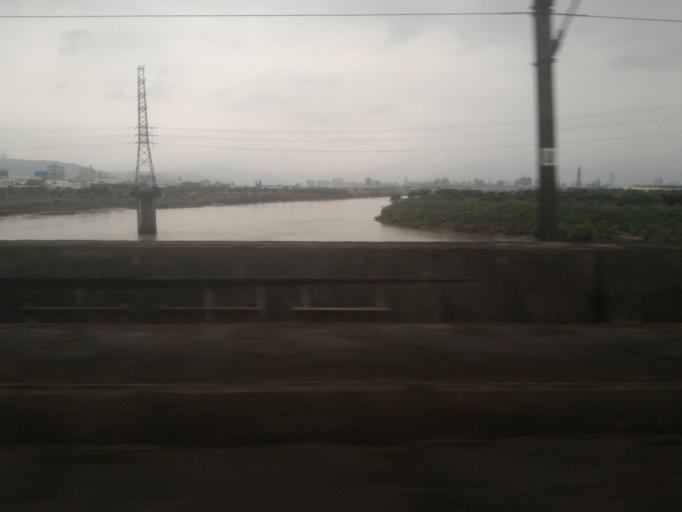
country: TW
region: Taipei
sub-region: Taipei
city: Banqiao
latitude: 25.0048
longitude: 121.4383
